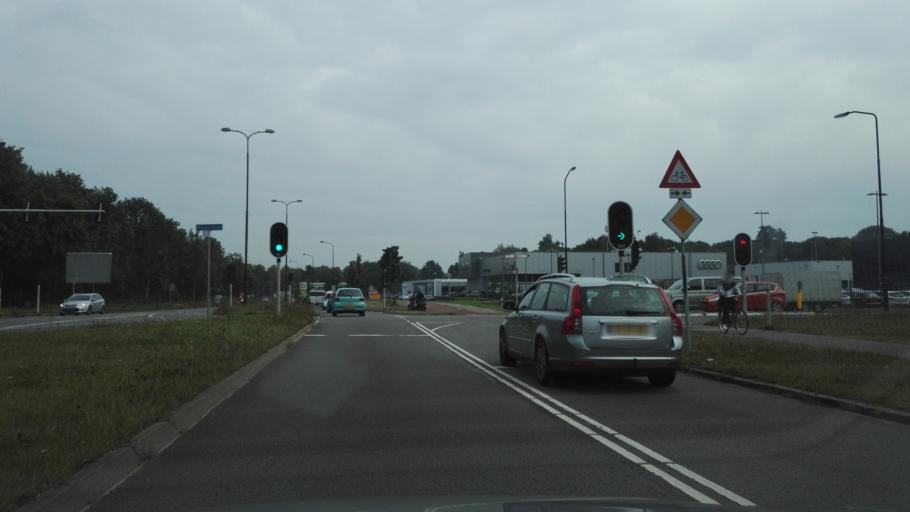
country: NL
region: Gelderland
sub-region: Gemeente Apeldoorn
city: Apeldoorn
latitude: 52.1935
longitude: 5.9828
